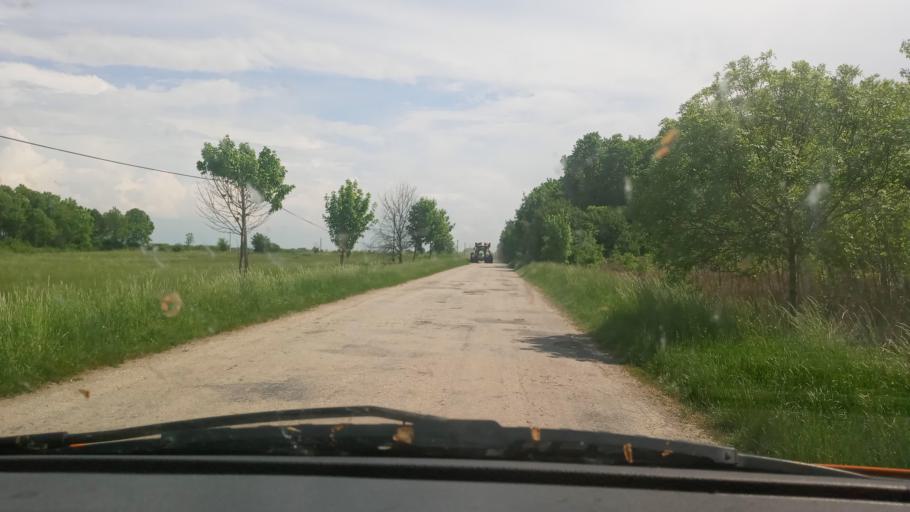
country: HU
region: Baranya
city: Siklos
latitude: 45.8054
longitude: 18.3439
